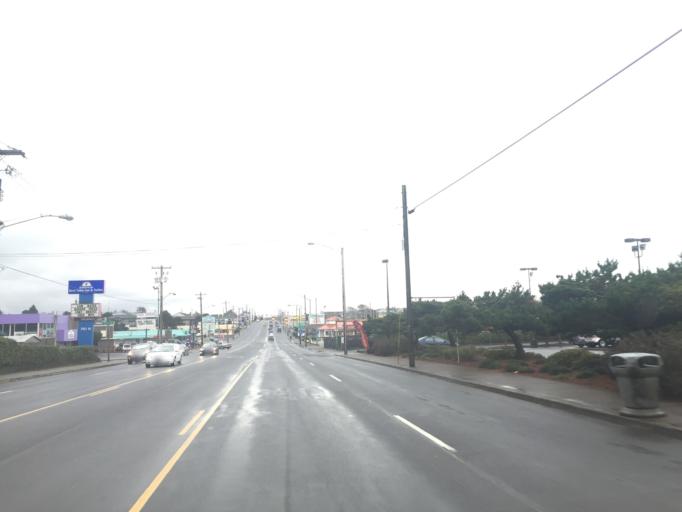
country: US
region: Oregon
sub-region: Lincoln County
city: Newport
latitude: 44.6418
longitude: -124.0531
